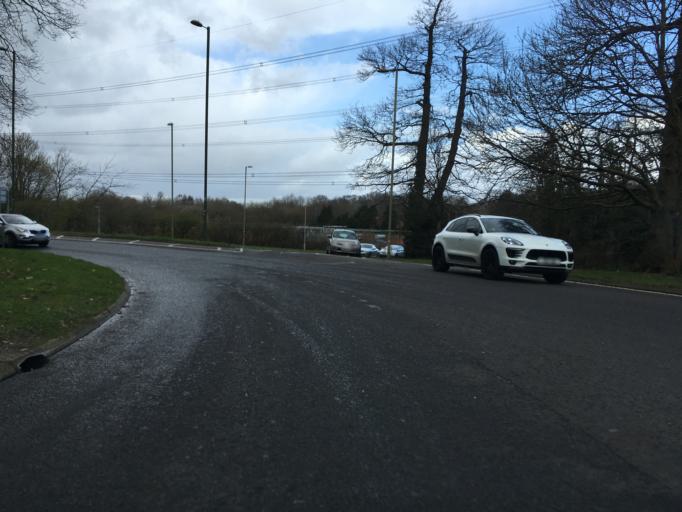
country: GB
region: England
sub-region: Hampshire
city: Eastleigh
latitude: 50.9697
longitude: -1.3895
